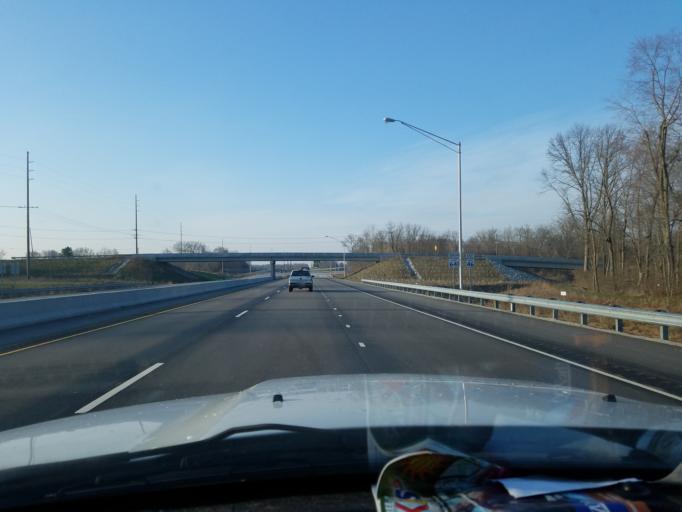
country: US
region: Indiana
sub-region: Vigo County
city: Terre Haute
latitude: 39.4206
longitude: -87.3331
